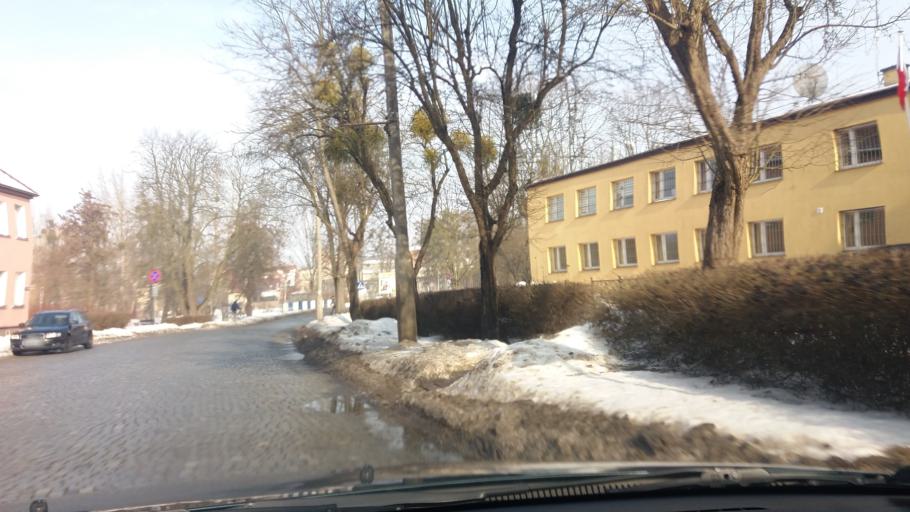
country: PL
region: Warmian-Masurian Voivodeship
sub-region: Powiat szczycienski
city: Szczytno
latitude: 53.5675
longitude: 20.9907
